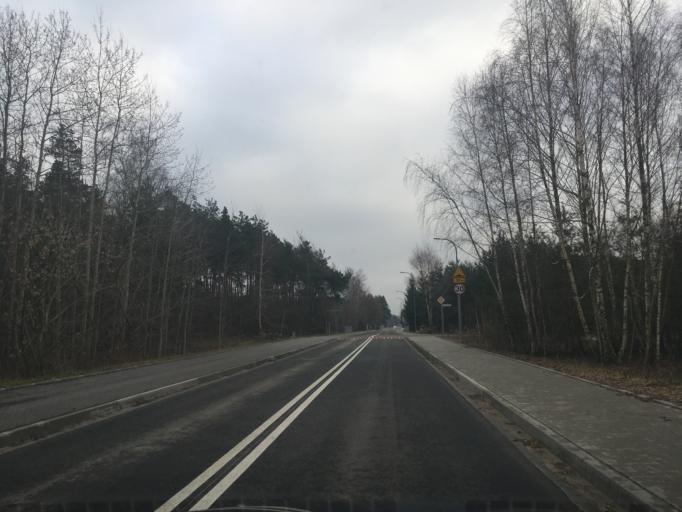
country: PL
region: Masovian Voivodeship
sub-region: Powiat piaseczynski
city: Lesznowola
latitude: 52.0651
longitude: 20.9748
